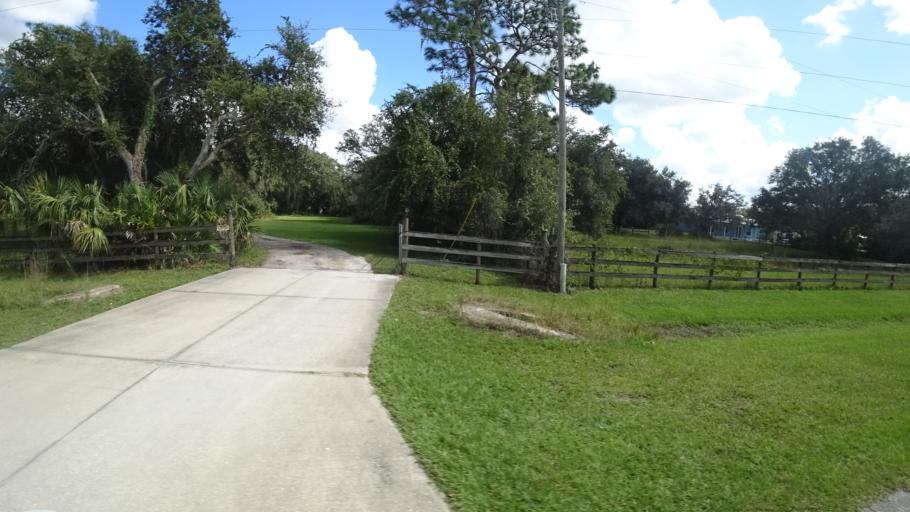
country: US
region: Florida
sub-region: Sarasota County
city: Lake Sarasota
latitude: 27.2841
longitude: -82.2231
